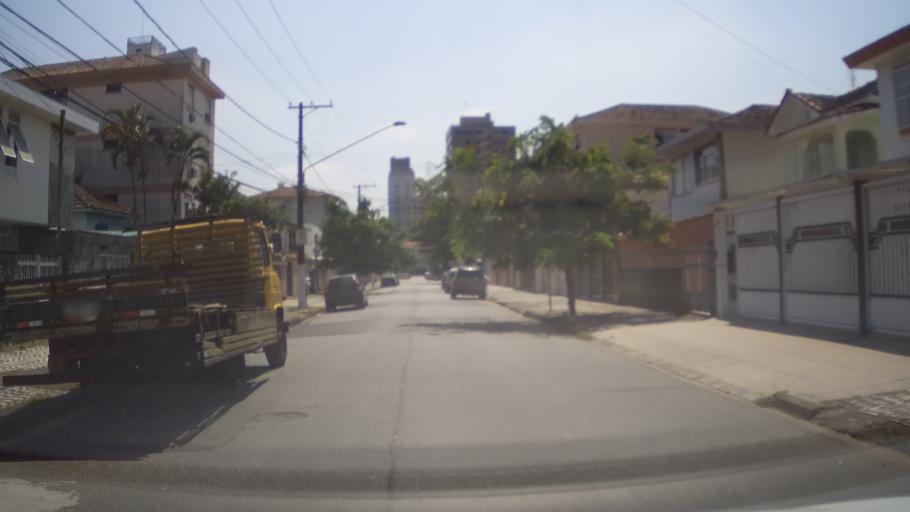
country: BR
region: Sao Paulo
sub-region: Santos
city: Santos
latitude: -23.9768
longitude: -46.3056
